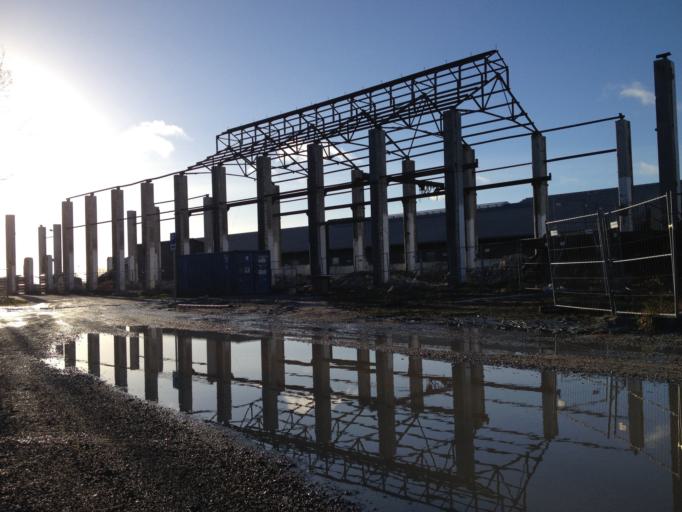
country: SE
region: Skane
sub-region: Malmo
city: Bunkeflostrand
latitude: 55.5241
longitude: 12.9186
